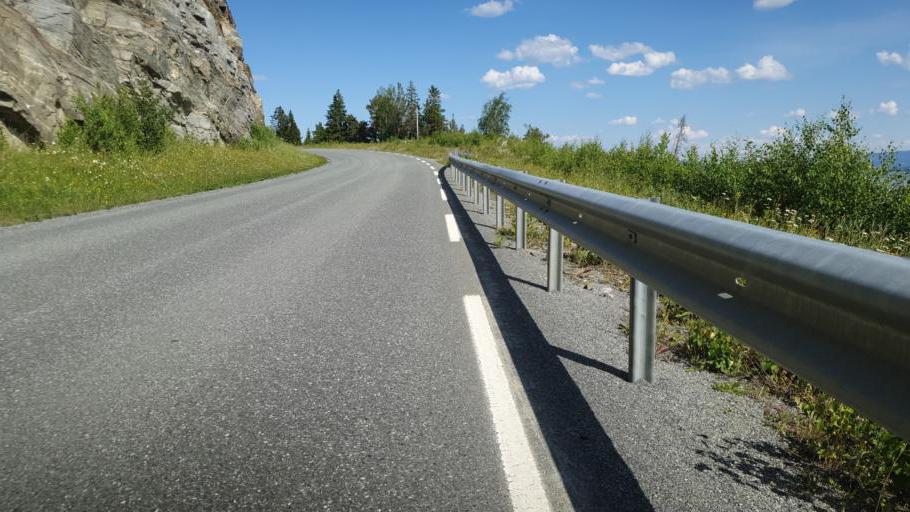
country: NO
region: Nord-Trondelag
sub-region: Leksvik
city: Leksvik
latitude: 63.6104
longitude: 10.5019
